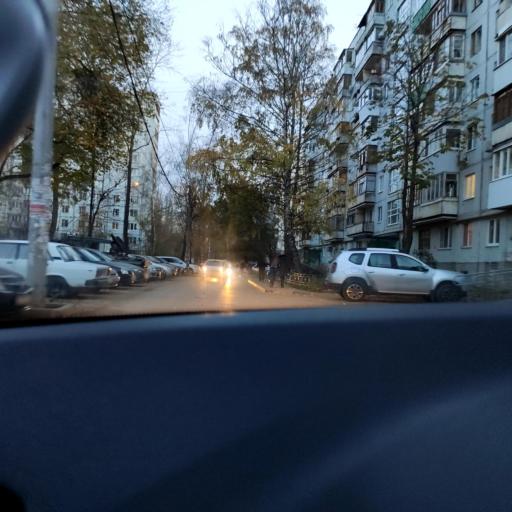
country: RU
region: Samara
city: Samara
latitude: 53.2413
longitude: 50.2135
